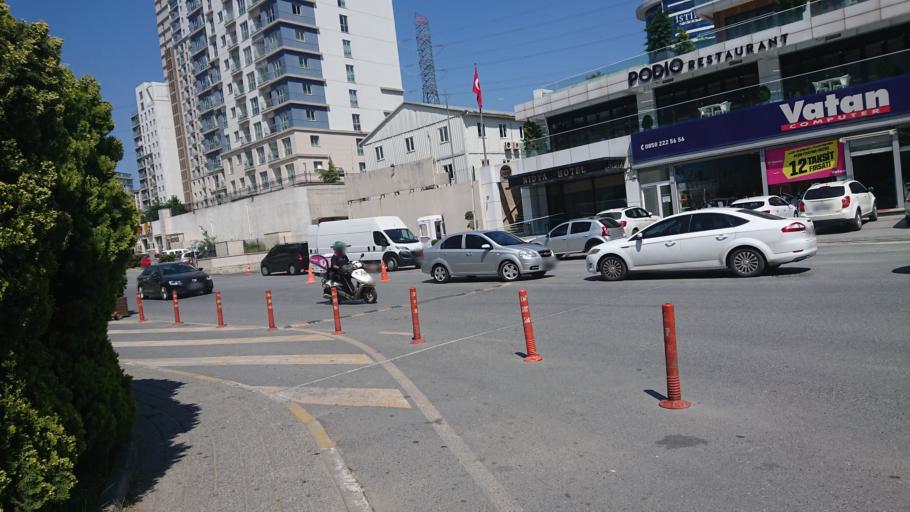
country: TR
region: Istanbul
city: Esenyurt
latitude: 41.0566
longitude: 28.6690
